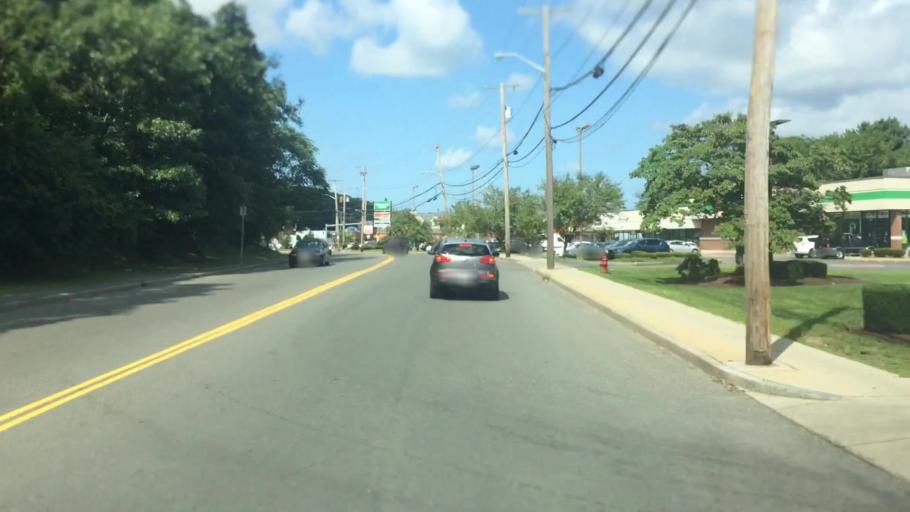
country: US
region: Massachusetts
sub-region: Essex County
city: Lynn
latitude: 42.4751
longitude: -70.9579
